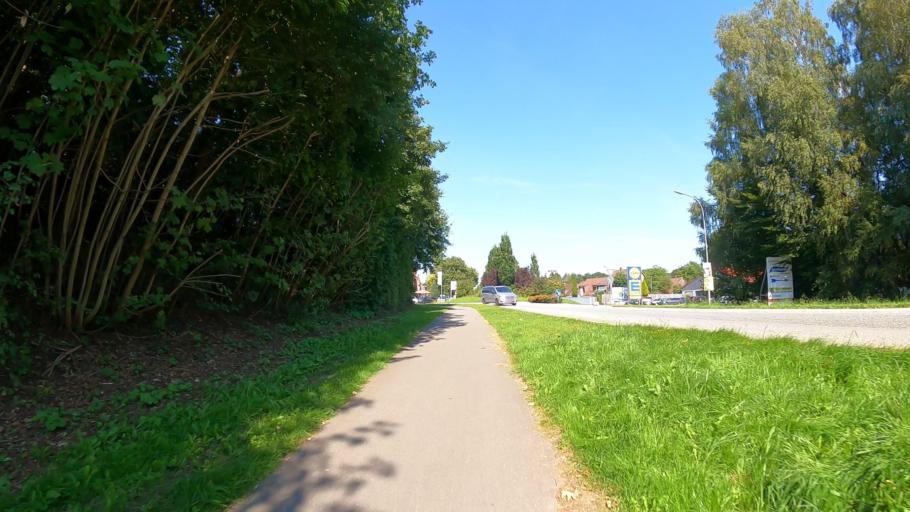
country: DE
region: Schleswig-Holstein
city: Bad Bramstedt
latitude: 53.9073
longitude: 9.8821
